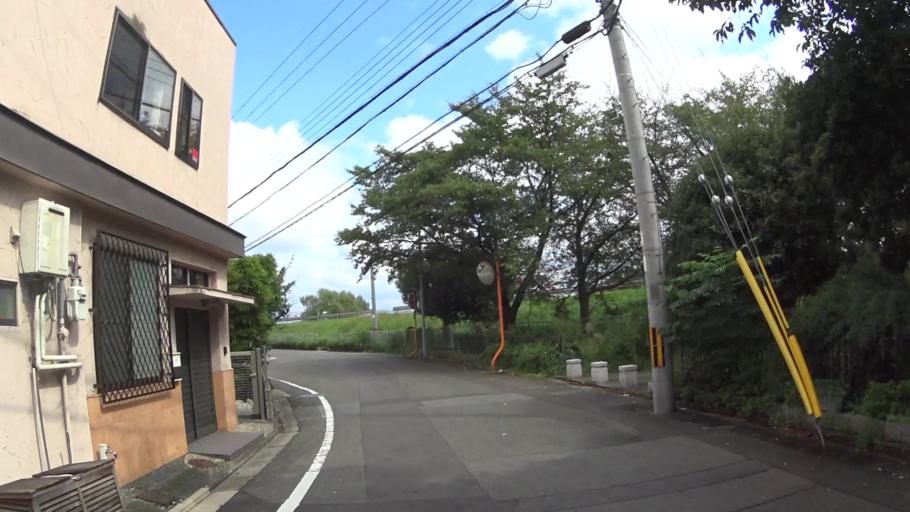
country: JP
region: Kyoto
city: Muko
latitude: 34.9620
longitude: 135.7213
